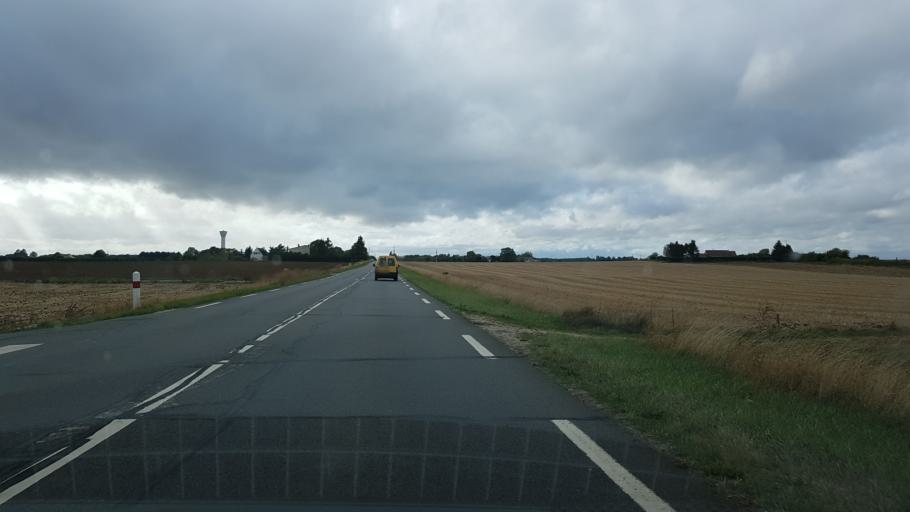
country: FR
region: Centre
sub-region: Departement du Loiret
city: Saint-Maurice-sur-Fessard
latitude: 47.9951
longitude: 2.6123
